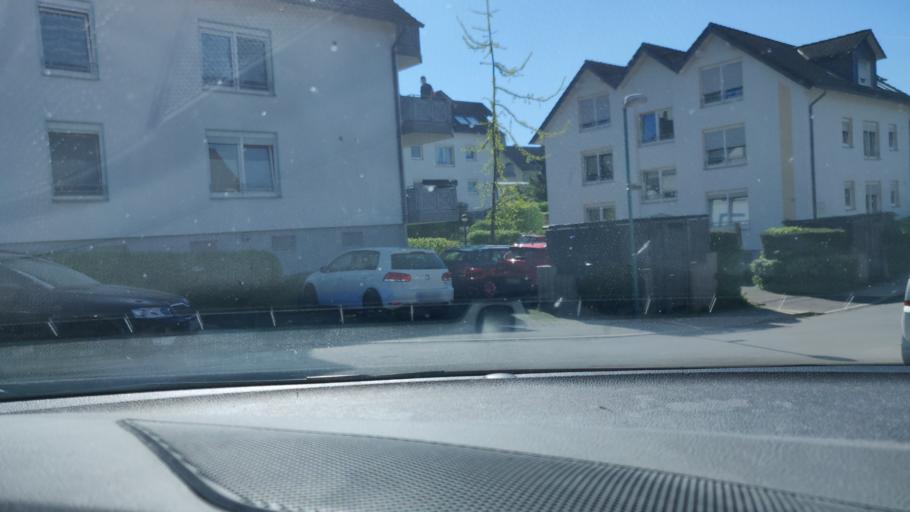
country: DE
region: North Rhine-Westphalia
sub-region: Regierungsbezirk Dusseldorf
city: Velbert
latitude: 51.3231
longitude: 7.0125
